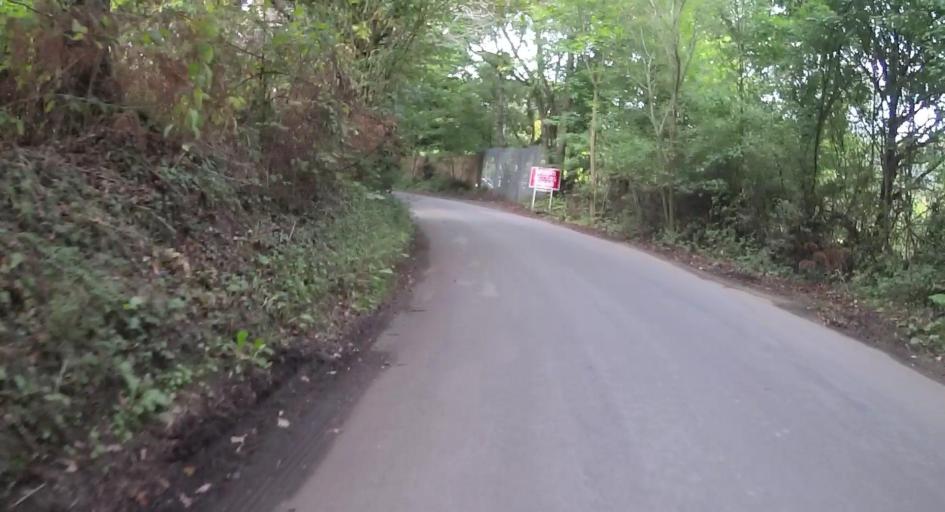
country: GB
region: England
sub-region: Surrey
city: Windlesham
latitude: 51.3486
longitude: -0.6469
